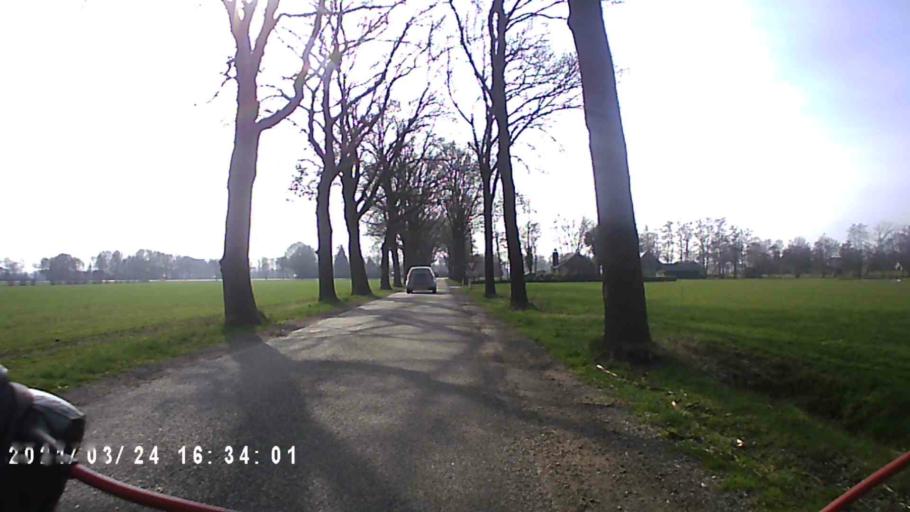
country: NL
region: Groningen
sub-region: Gemeente Leek
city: Leek
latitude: 53.0688
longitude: 6.2753
